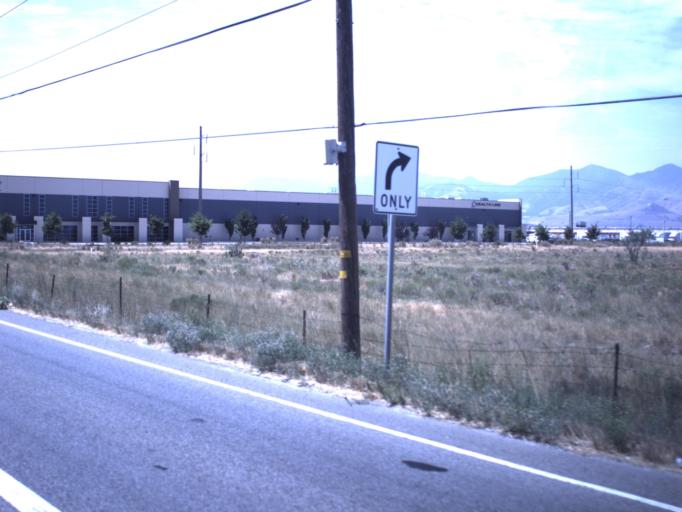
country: US
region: Utah
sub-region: Salt Lake County
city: West Valley City
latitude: 40.7632
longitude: -112.0251
